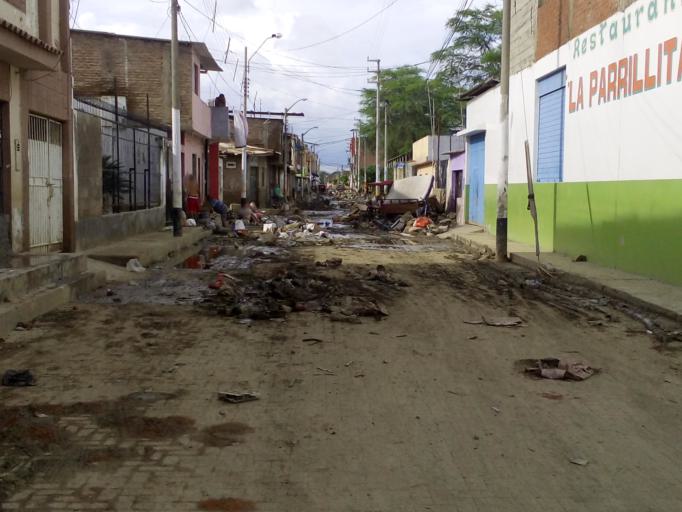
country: PE
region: Piura
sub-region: Provincia de Piura
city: Catacaos
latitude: -5.2654
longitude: -80.6731
